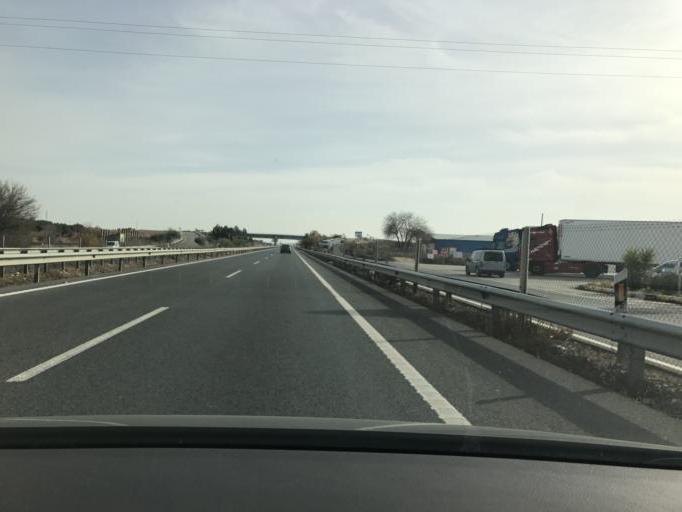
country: ES
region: Andalusia
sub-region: Provincia de Granada
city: Moraleda de Zafayona
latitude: 37.1829
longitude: -3.9525
